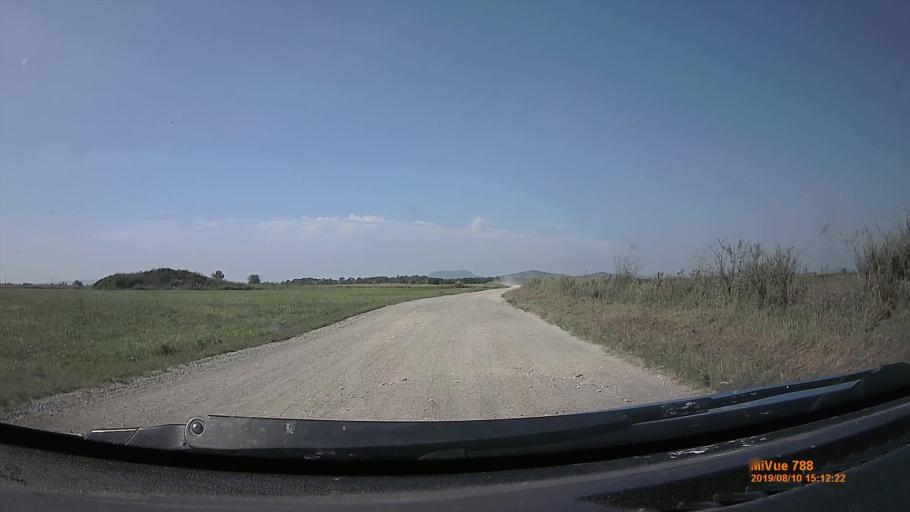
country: HU
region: Somogy
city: Fonyod
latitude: 46.6871
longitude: 17.5636
